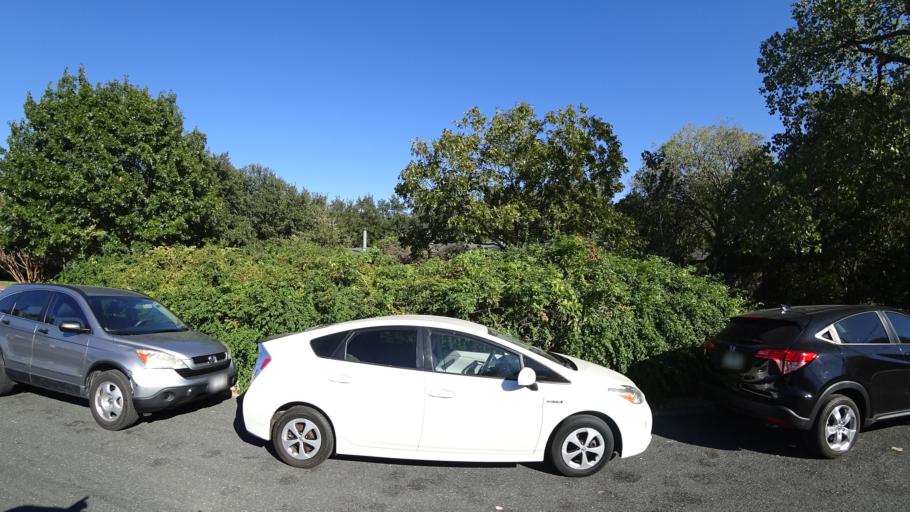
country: US
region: Texas
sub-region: Travis County
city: West Lake Hills
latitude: 30.3309
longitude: -97.7592
